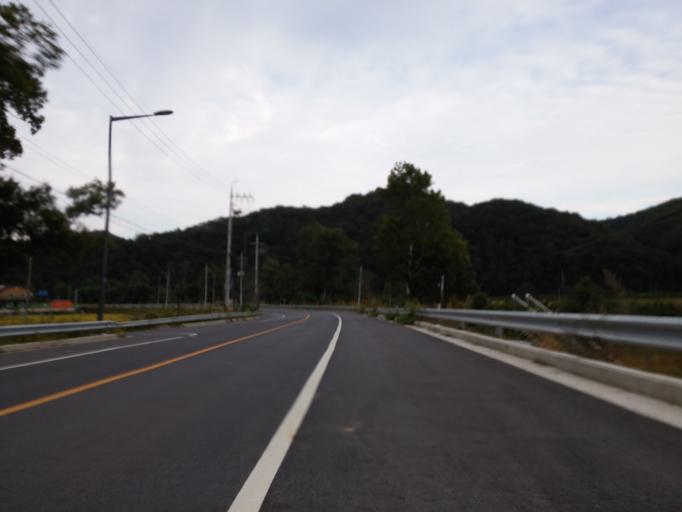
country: KR
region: Daejeon
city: Daejeon
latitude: 36.2218
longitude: 127.2992
